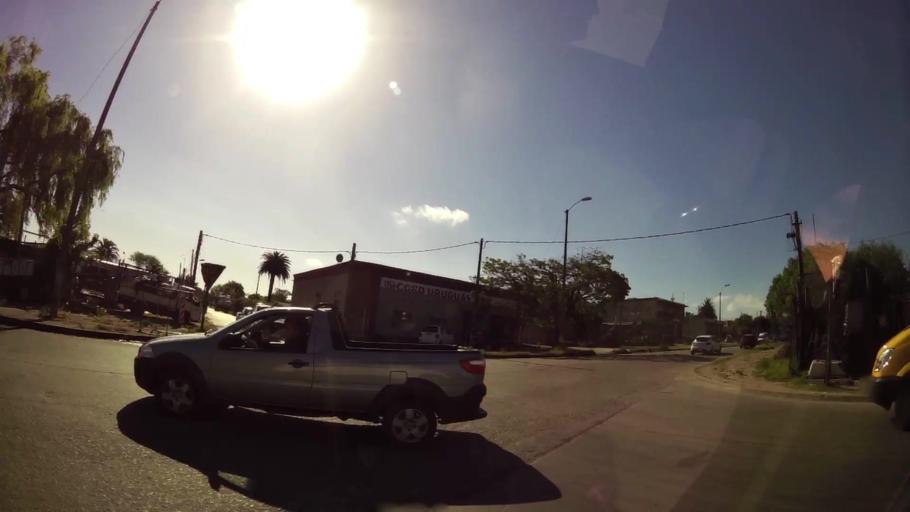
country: UY
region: Montevideo
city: Montevideo
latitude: -34.8315
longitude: -56.1540
